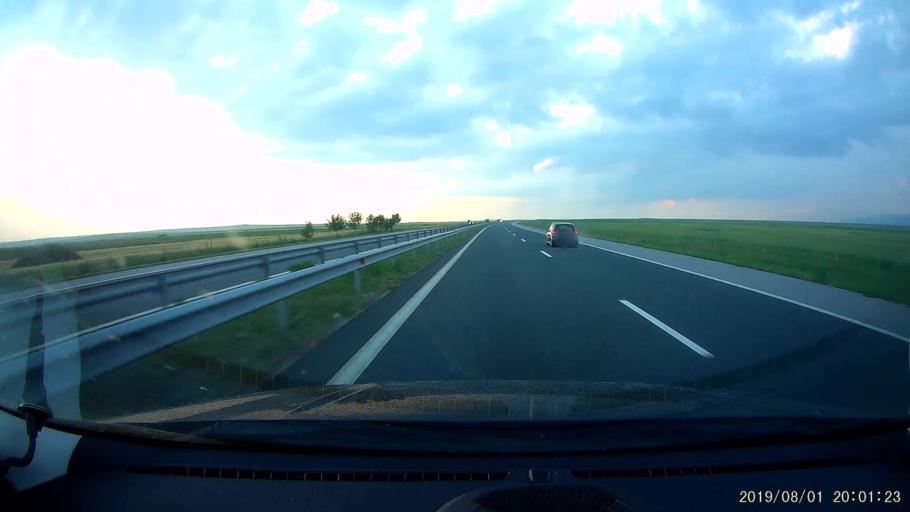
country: BG
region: Yambol
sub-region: Obshtina Straldzha
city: Straldzha
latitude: 42.5563
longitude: 26.6678
